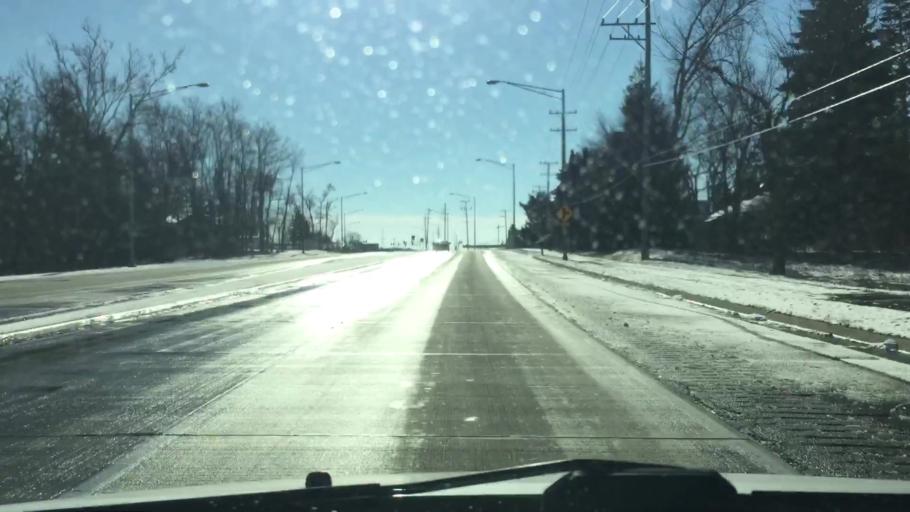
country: US
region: Illinois
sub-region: Kane County
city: Geneva
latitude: 41.8901
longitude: -88.2772
